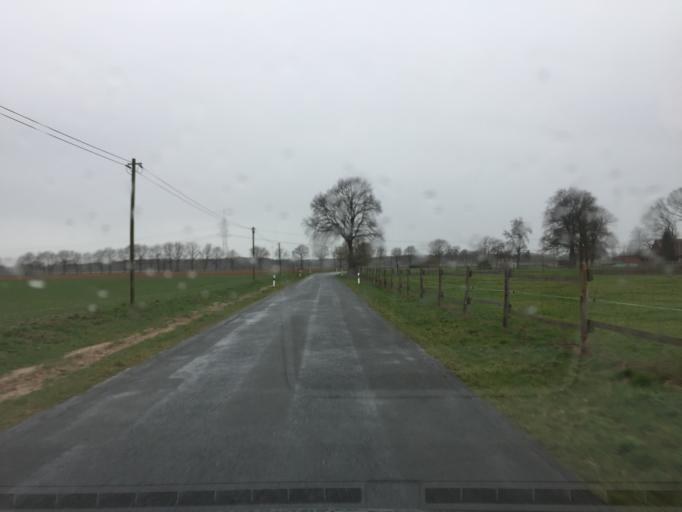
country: DE
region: Lower Saxony
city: Steyerberg
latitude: 52.5313
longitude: 9.0063
